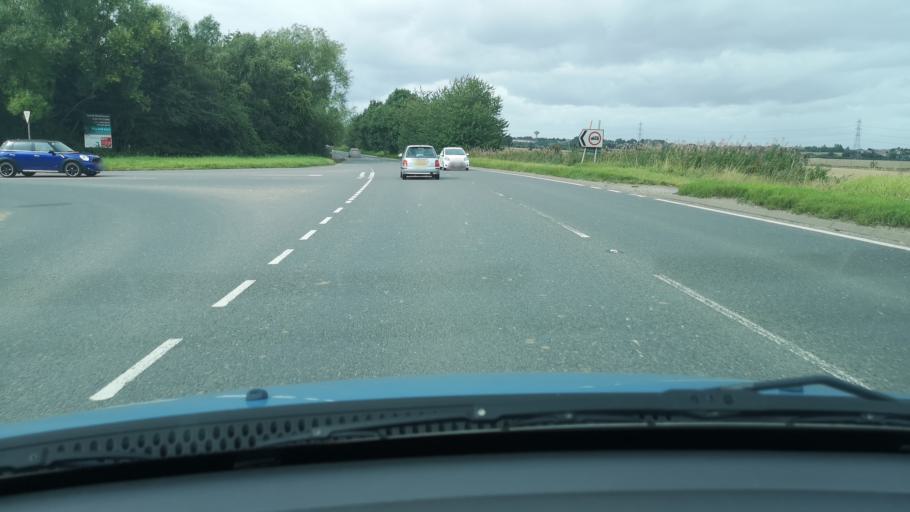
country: GB
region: England
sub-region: City and Borough of Wakefield
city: South Elmsall
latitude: 53.6010
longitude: -1.2606
